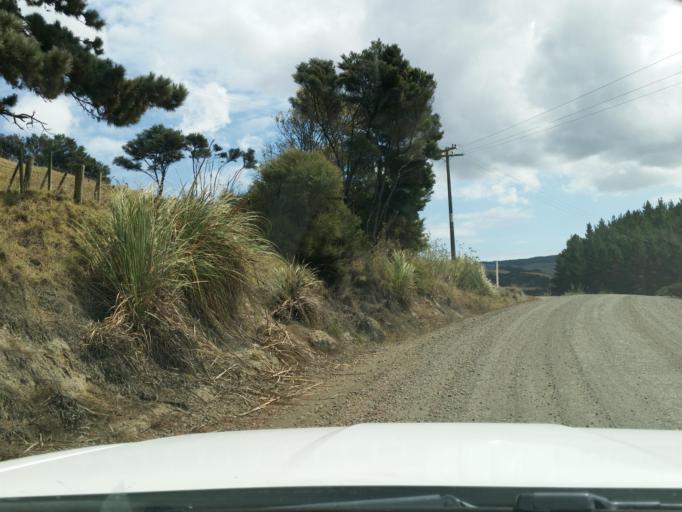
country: NZ
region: Auckland
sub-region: Auckland
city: Wellsford
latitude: -36.3015
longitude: 174.1118
